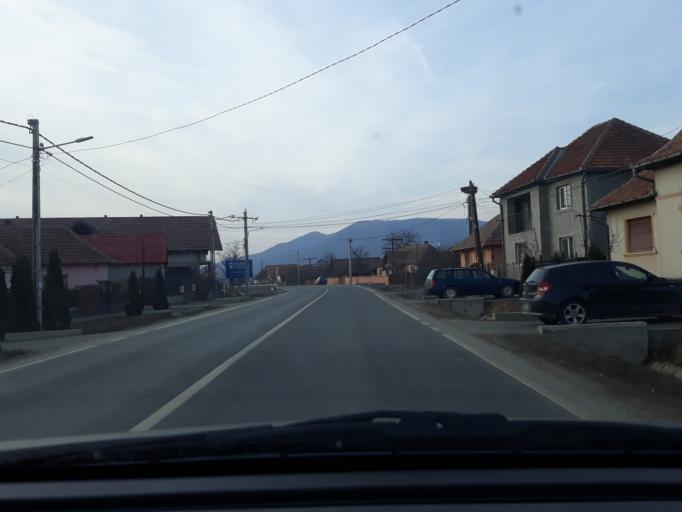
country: RO
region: Salaj
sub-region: Comuna Periceiu
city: Periceiu
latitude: 47.2270
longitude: 22.8583
